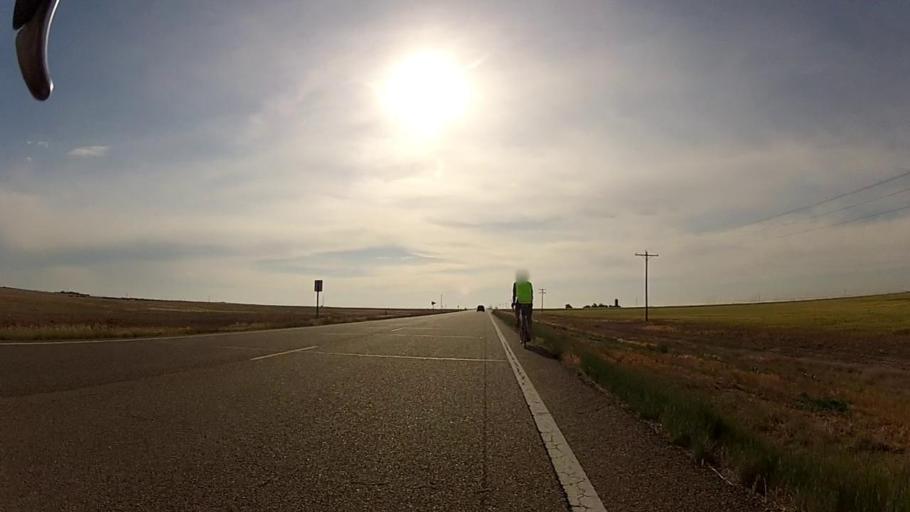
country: US
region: Kansas
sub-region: Grant County
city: Ulysses
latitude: 37.5766
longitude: -101.4564
